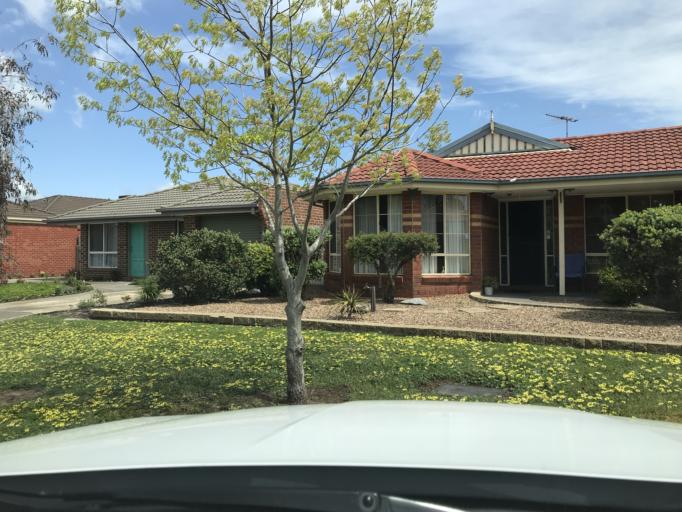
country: AU
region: Victoria
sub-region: Hume
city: Craigieburn
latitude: -37.6135
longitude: 144.9386
